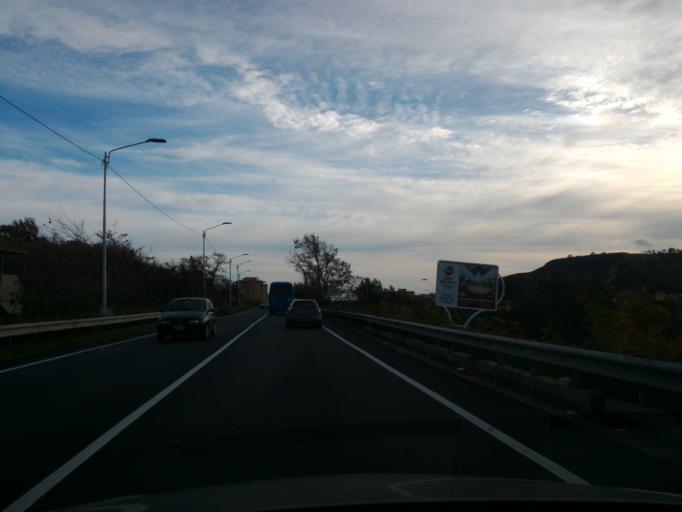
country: IT
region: Calabria
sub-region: Provincia di Catanzaro
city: Catanzaro
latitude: 38.8748
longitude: 16.6045
